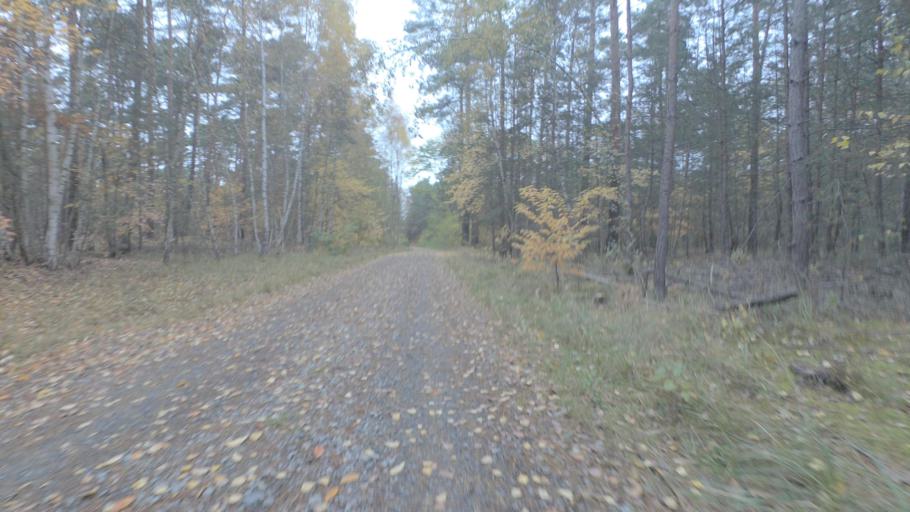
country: DE
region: Brandenburg
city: Rangsdorf
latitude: 52.3154
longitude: 13.4079
